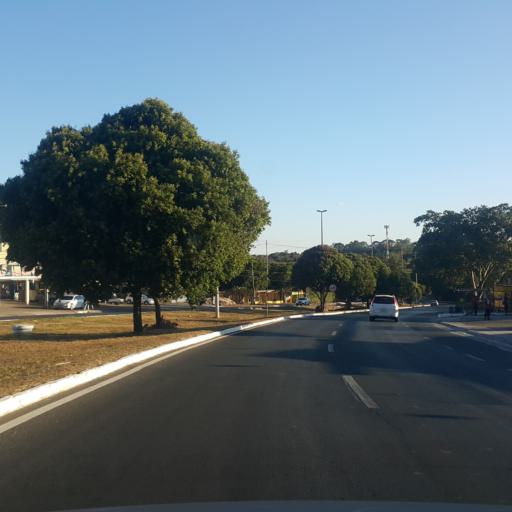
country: BR
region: Federal District
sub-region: Brasilia
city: Brasilia
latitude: -15.8552
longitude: -47.9754
